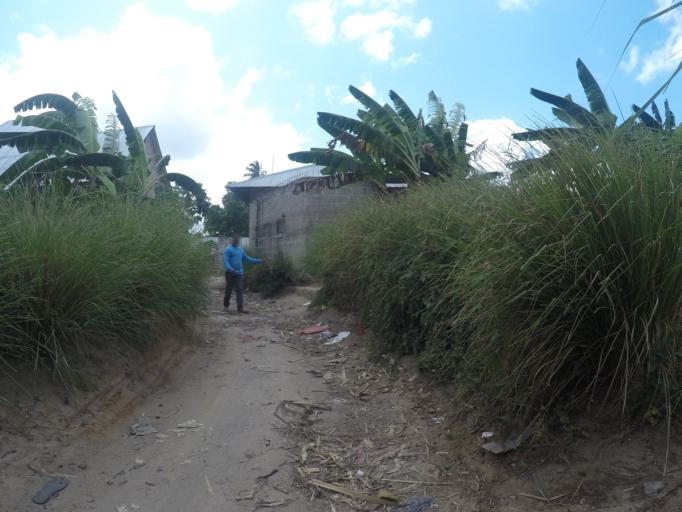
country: TZ
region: Zanzibar Urban/West
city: Zanzibar
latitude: -6.2053
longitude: 39.2419
